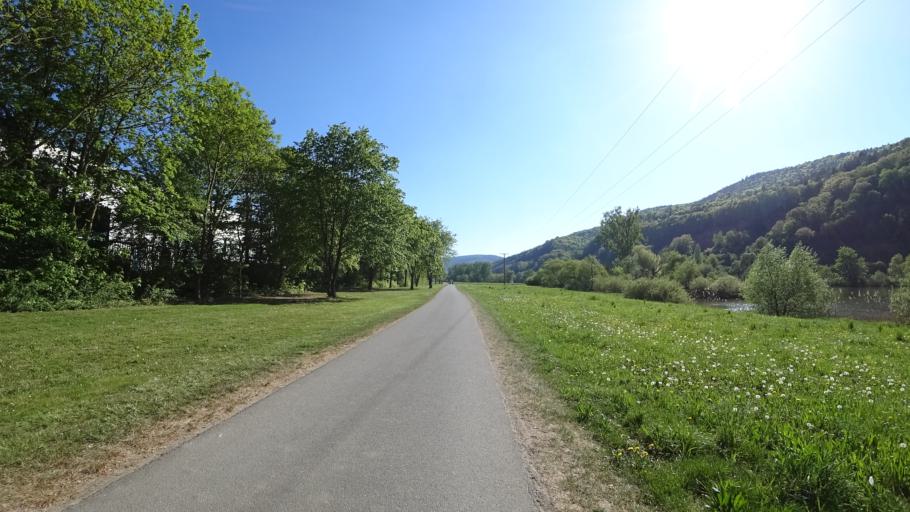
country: DE
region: Bavaria
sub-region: Regierungsbezirk Unterfranken
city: Burgstadt
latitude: 49.7311
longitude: 9.2713
